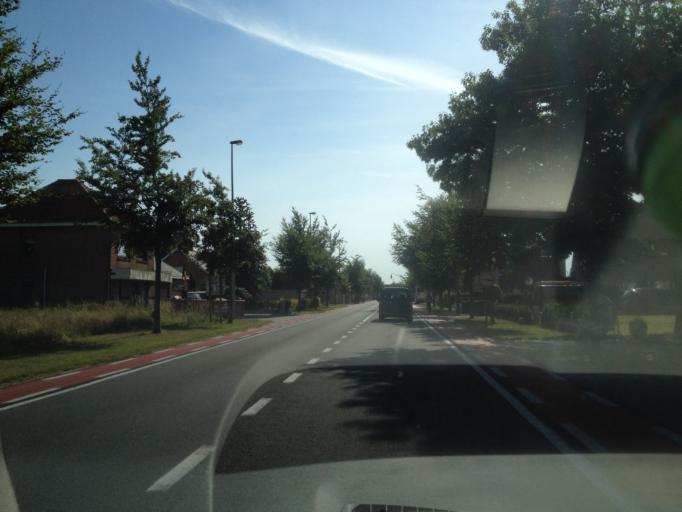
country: BE
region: Flanders
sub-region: Provincie West-Vlaanderen
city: Jabbeke
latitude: 51.1731
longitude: 3.0616
